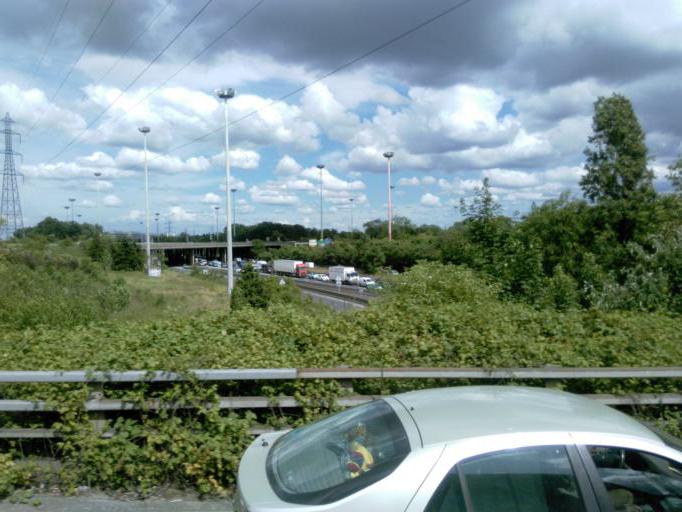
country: FR
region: Ile-de-France
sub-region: Departement des Hauts-de-Seine
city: Gennevilliers
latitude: 48.9379
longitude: 2.2940
